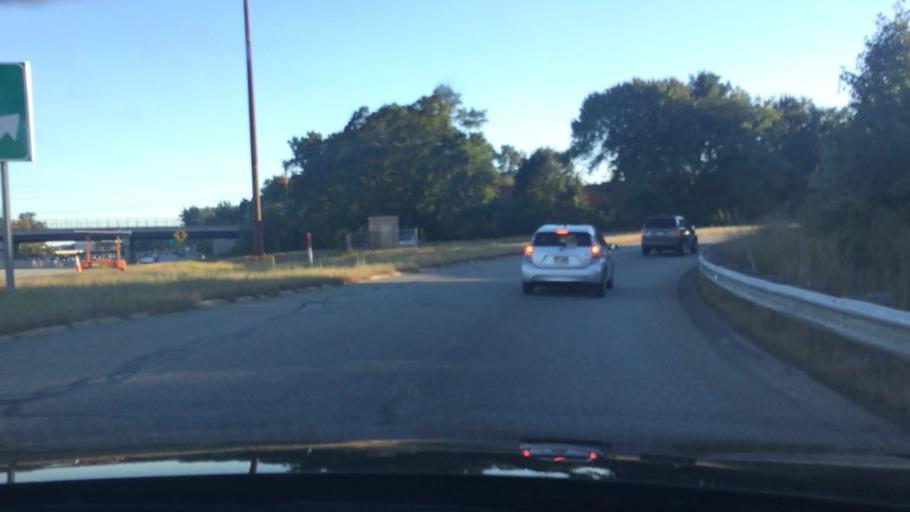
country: US
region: Massachusetts
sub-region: Middlesex County
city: Lowell
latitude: 42.6065
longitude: -71.3258
